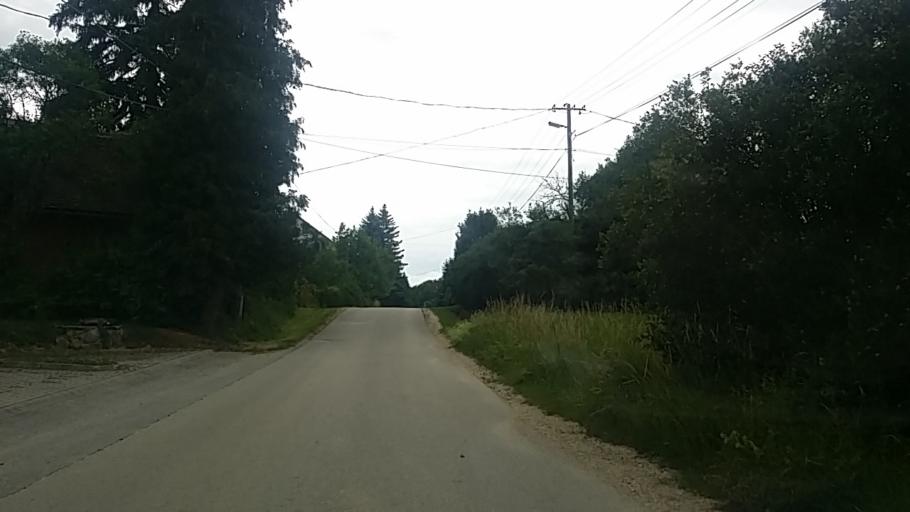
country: SI
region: Hodos-Hodos
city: Hodos
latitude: 46.8476
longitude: 16.4135
